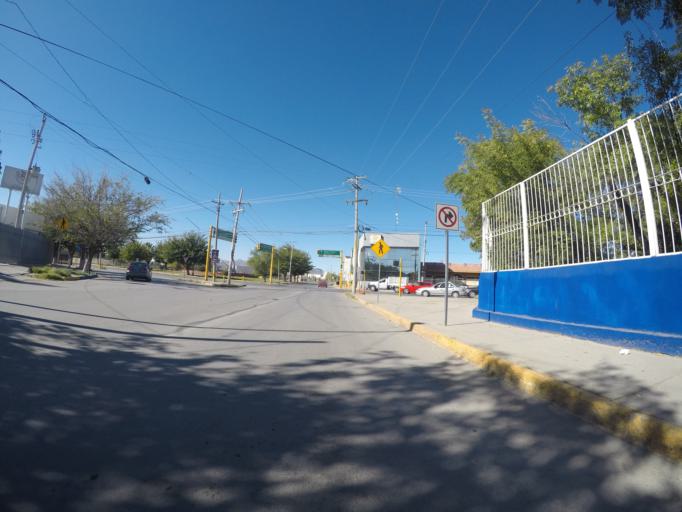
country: MX
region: Chihuahua
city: Ciudad Juarez
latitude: 31.7436
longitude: -106.4485
